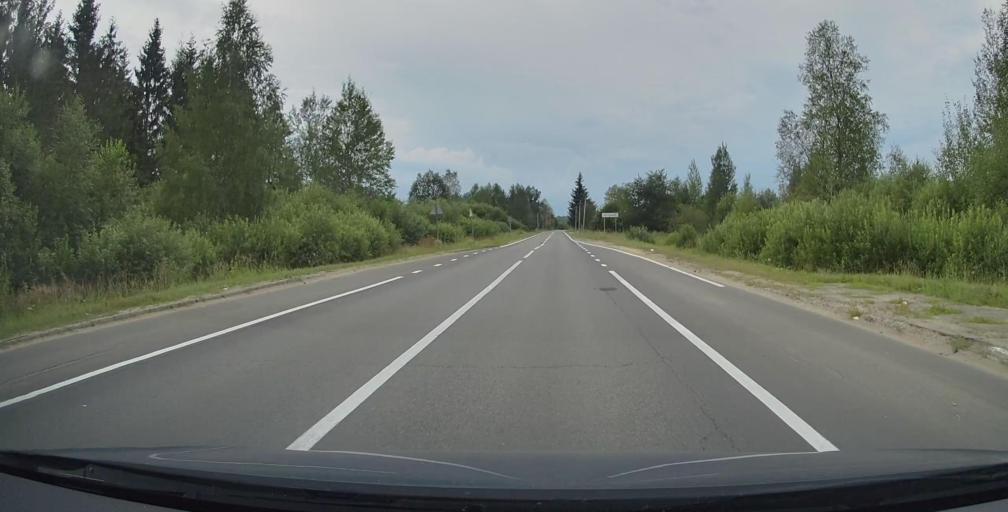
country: RU
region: Jaroslavl
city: Rybinsk
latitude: 57.9453
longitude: 38.7024
